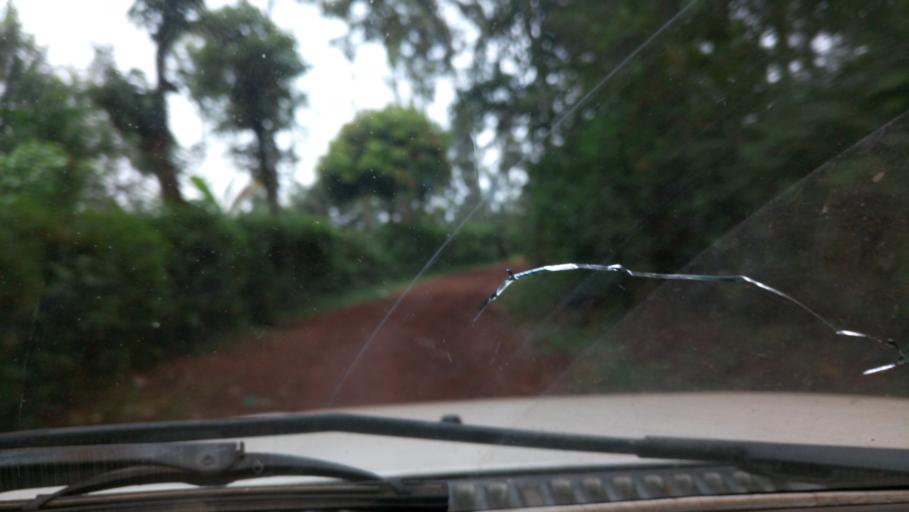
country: KE
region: Murang'a District
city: Kangema
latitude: -0.6765
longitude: 37.0141
